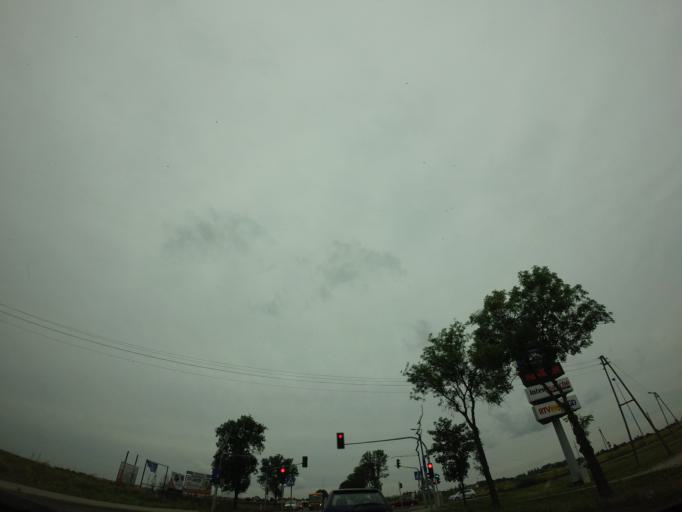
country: PL
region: Masovian Voivodeship
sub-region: Powiat ciechanowski
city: Ciechanow
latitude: 52.8807
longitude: 20.6544
